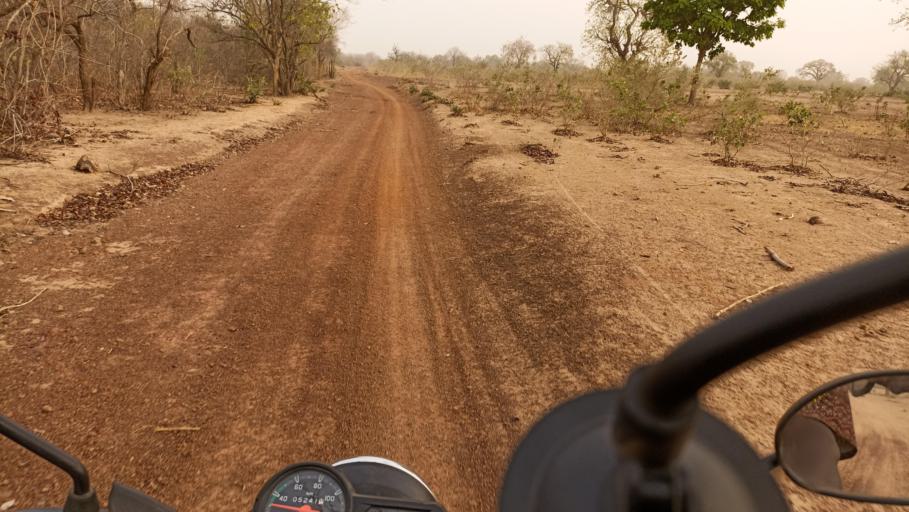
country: BF
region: Boucle du Mouhoun
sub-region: Province du Nayala
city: Toma
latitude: 12.8977
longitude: -2.7878
